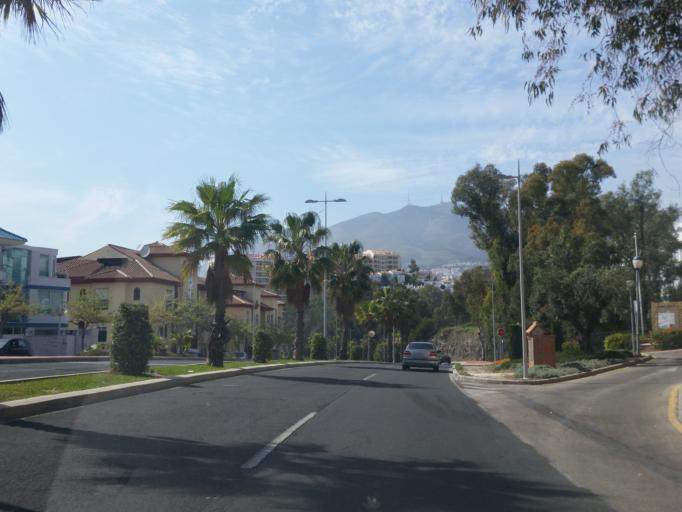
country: ES
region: Andalusia
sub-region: Provincia de Malaga
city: Benalmadena
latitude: 36.5808
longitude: -4.5464
